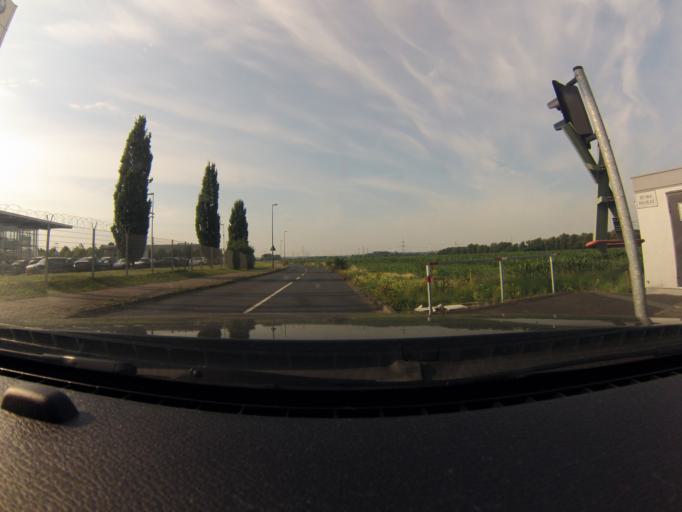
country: DE
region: North Rhine-Westphalia
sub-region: Regierungsbezirk Koln
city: Frechen
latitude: 50.9156
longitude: 6.8514
